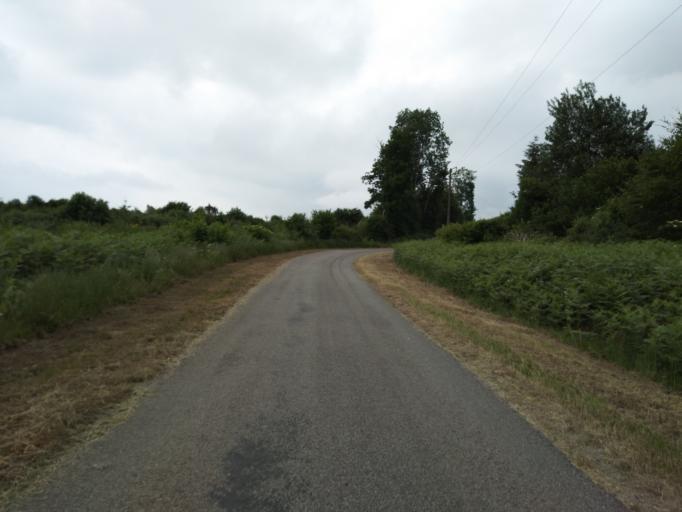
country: FR
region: Bourgogne
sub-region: Departement de la Cote-d'Or
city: Saulieu
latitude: 47.2871
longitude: 4.1299
